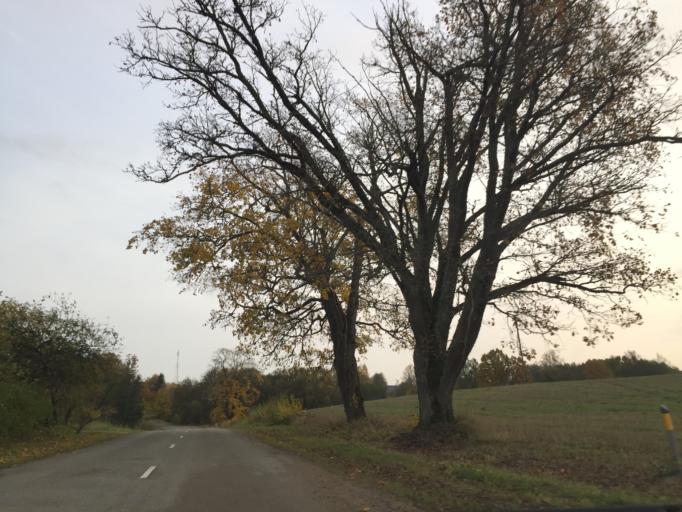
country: LV
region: Pargaujas
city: Stalbe
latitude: 57.3173
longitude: 25.1436
